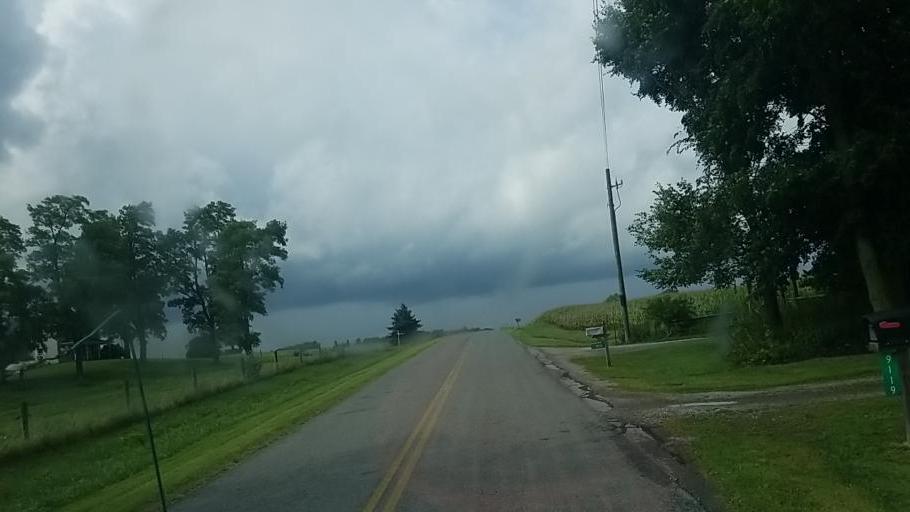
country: US
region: Ohio
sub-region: Champaign County
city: North Lewisburg
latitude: 40.2489
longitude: -83.6502
